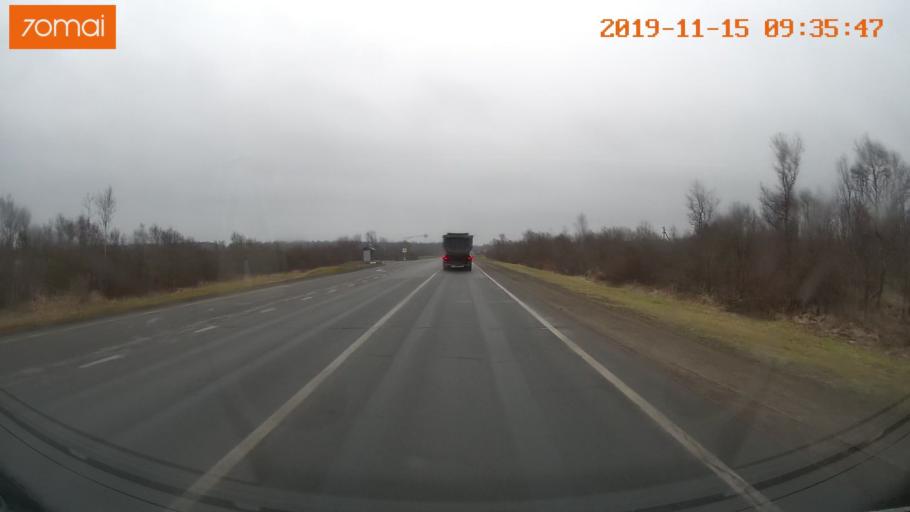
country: RU
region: Vologda
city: Sheksna
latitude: 59.2523
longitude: 38.4064
